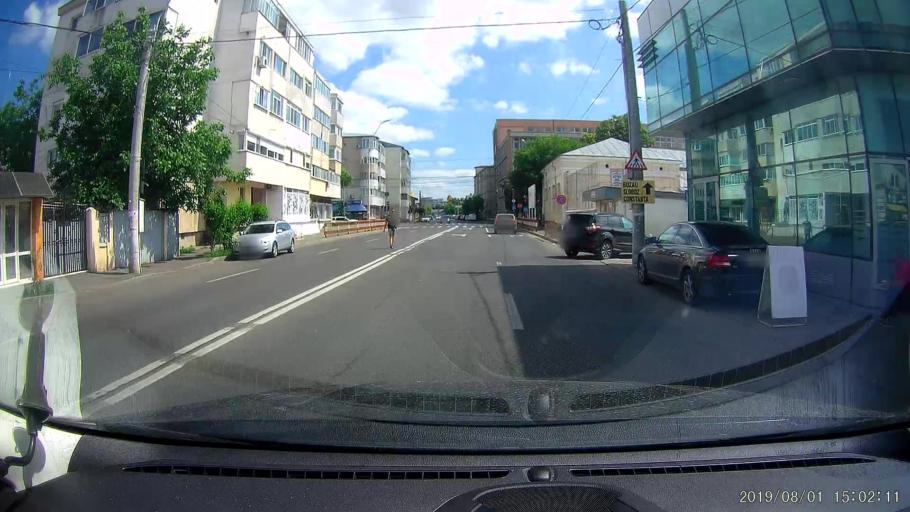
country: RO
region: Braila
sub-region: Municipiul Braila
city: Braila
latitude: 45.2670
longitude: 27.9612
